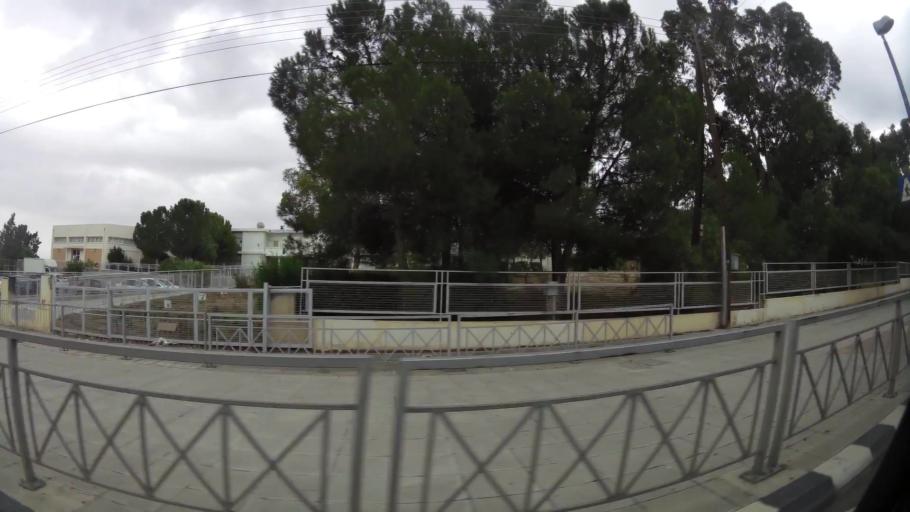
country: CY
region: Lefkosia
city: Geri
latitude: 35.1065
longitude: 33.3852
